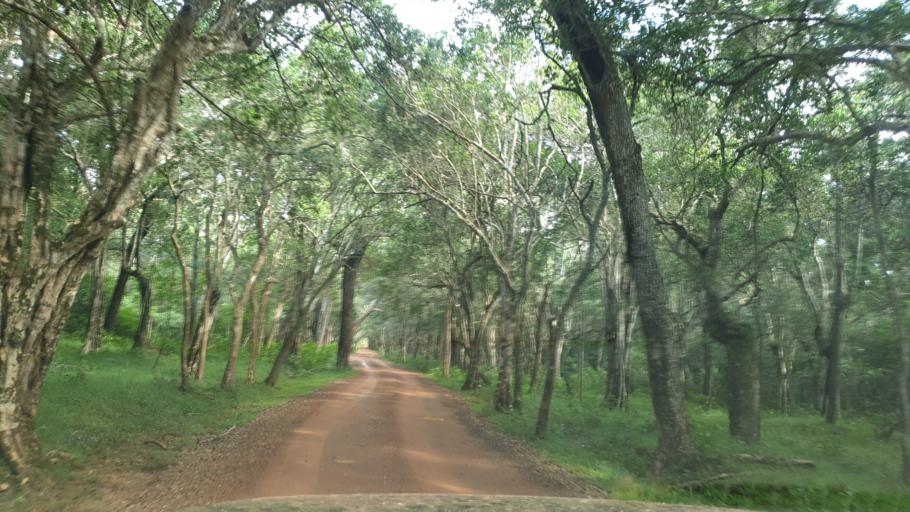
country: LK
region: North Central
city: Anuradhapura
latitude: 8.3805
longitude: 80.0651
